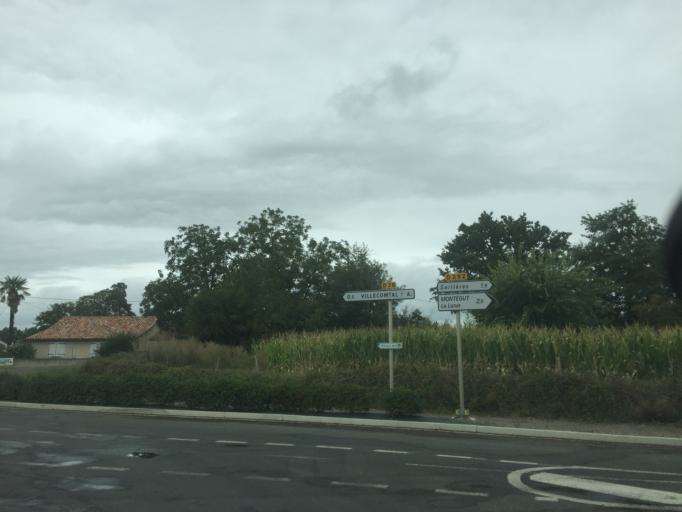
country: FR
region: Midi-Pyrenees
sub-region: Departement des Hautes-Pyrenees
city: Rabastens-de-Bigorre
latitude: 43.3991
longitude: 0.2027
